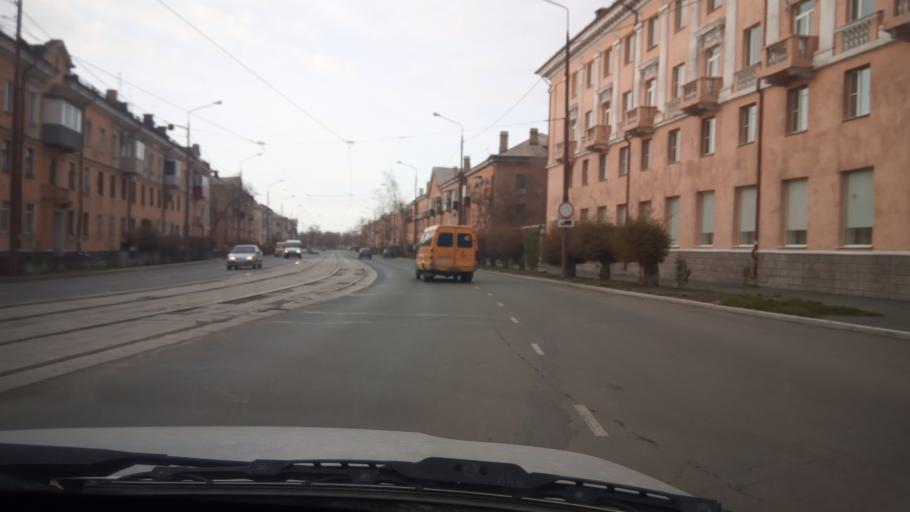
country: RU
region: Orenburg
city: Novotroitsk
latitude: 51.1990
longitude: 58.3338
